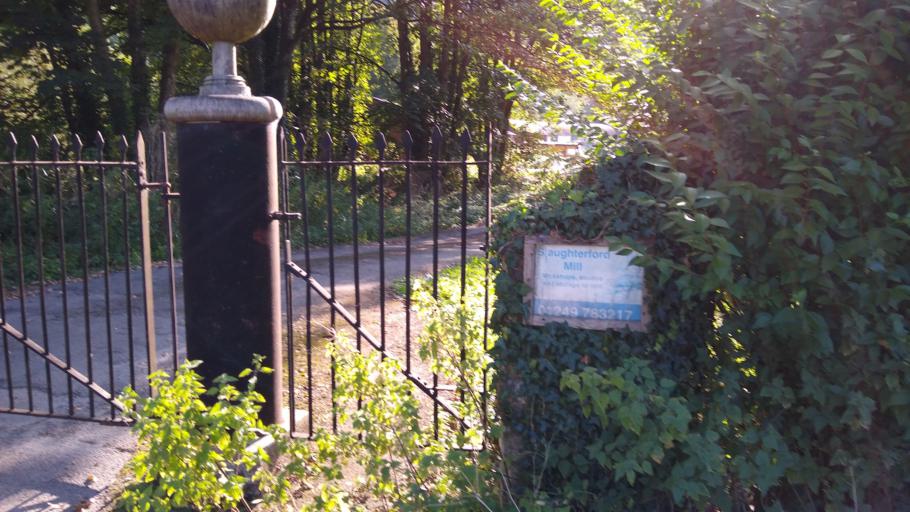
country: GB
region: England
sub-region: Wiltshire
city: Biddestone
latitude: 51.4632
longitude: -2.2296
